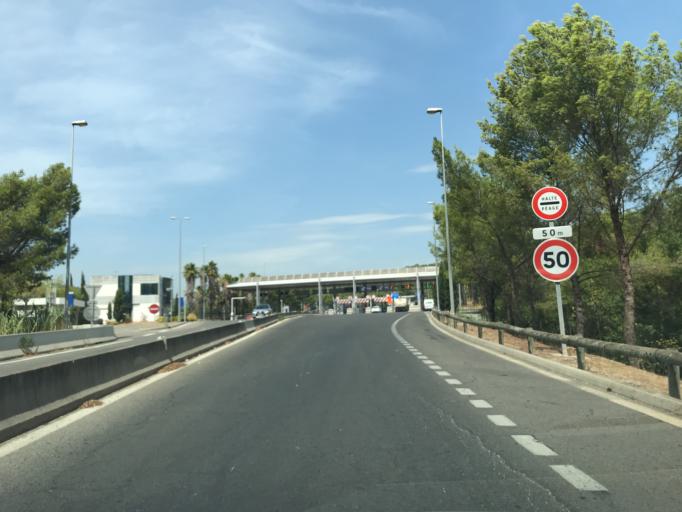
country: FR
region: Provence-Alpes-Cote d'Azur
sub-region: Departement du Var
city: Bandol
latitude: 43.1432
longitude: 5.7686
